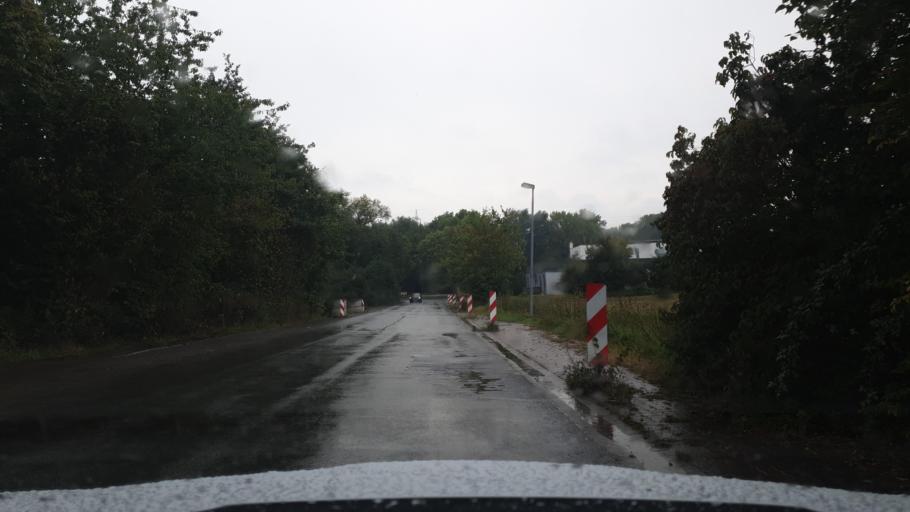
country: DE
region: North Rhine-Westphalia
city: Porta Westfalica
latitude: 52.2075
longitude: 8.8828
